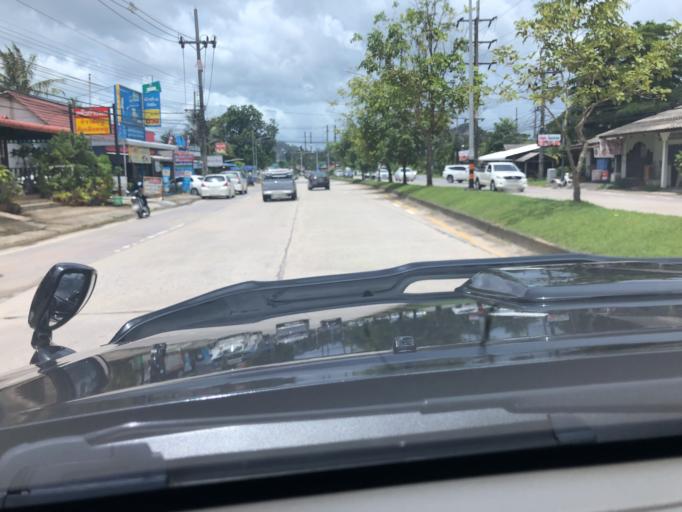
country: TH
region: Phangnga
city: Phang Nga
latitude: 8.4414
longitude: 98.5273
